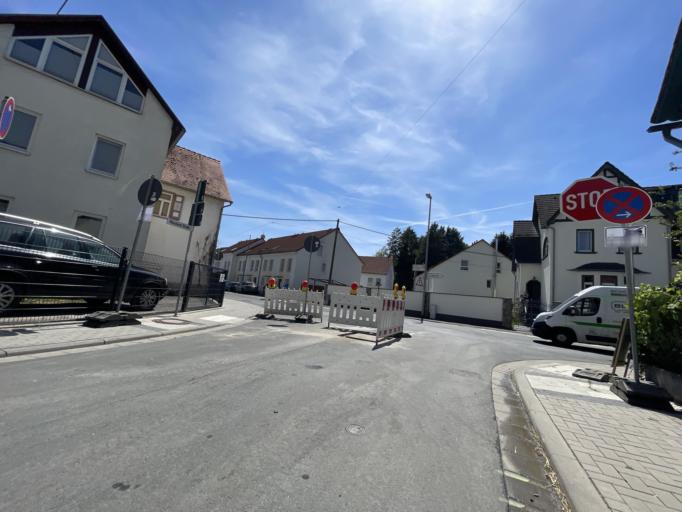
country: GB
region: England
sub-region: East Sussex
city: Eastbourne
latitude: 50.5892
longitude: 0.4550
